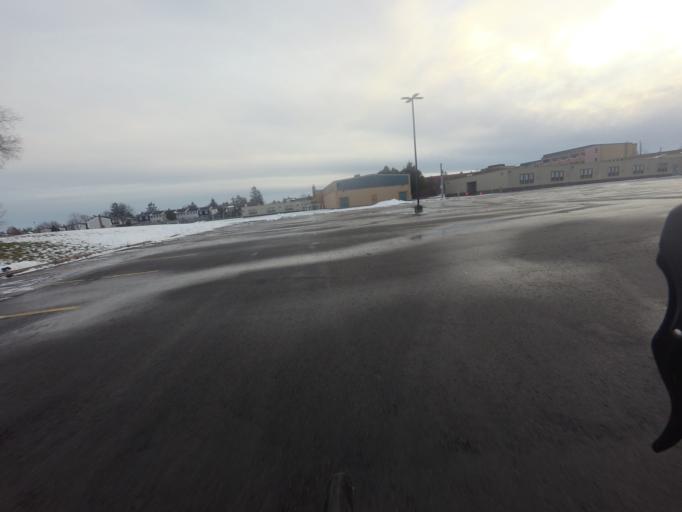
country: CA
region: Ontario
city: Ottawa
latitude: 45.3669
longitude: -75.7115
